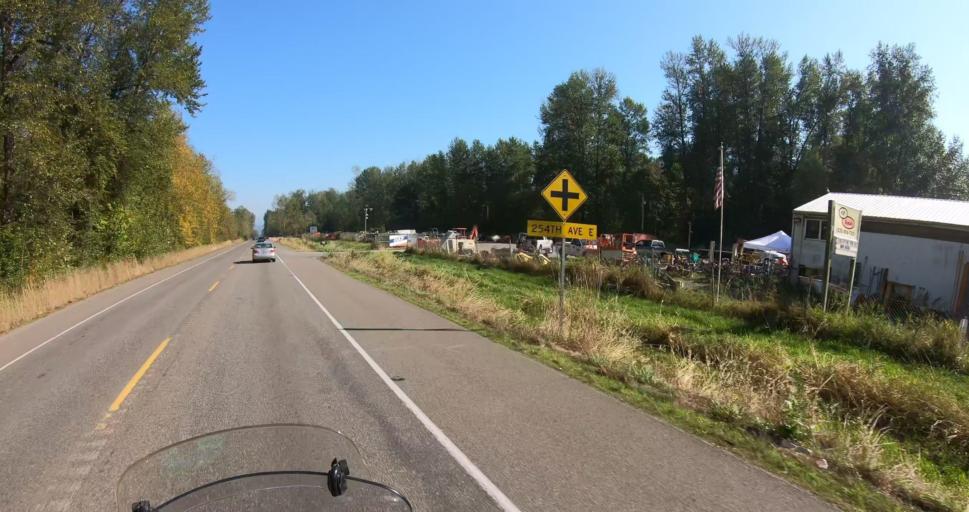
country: US
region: Washington
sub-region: Pierce County
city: Prairie Ridge
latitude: 47.1635
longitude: -122.0947
